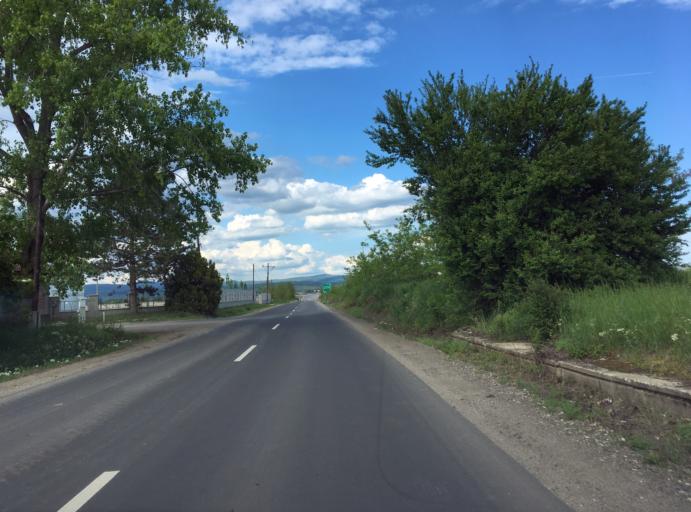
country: HU
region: Heves
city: Lorinci
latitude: 47.7272
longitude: 19.6598
